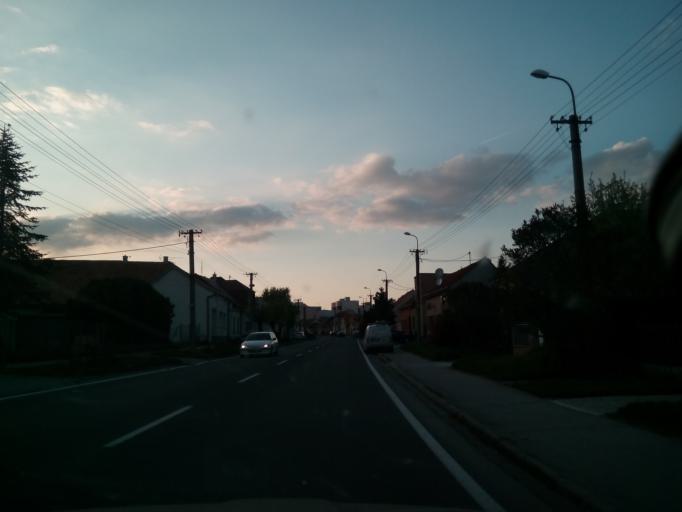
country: SK
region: Trnavsky
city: Vrbove
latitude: 48.6170
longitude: 17.7302
